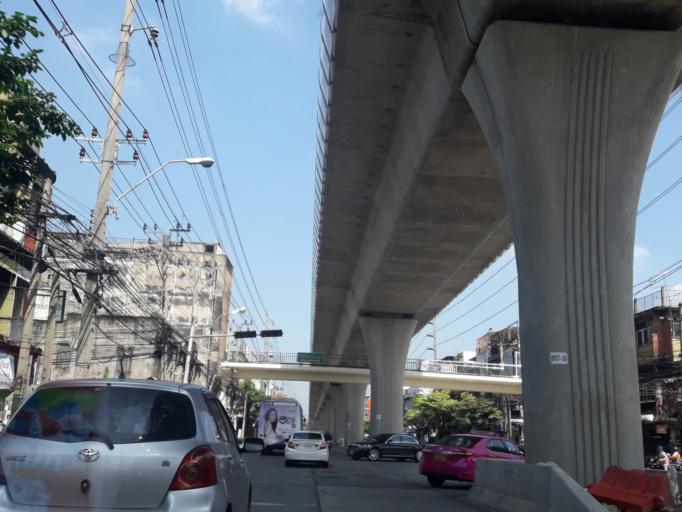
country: TH
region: Bangkok
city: Bangkok Noi
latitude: 13.7458
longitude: 100.4702
